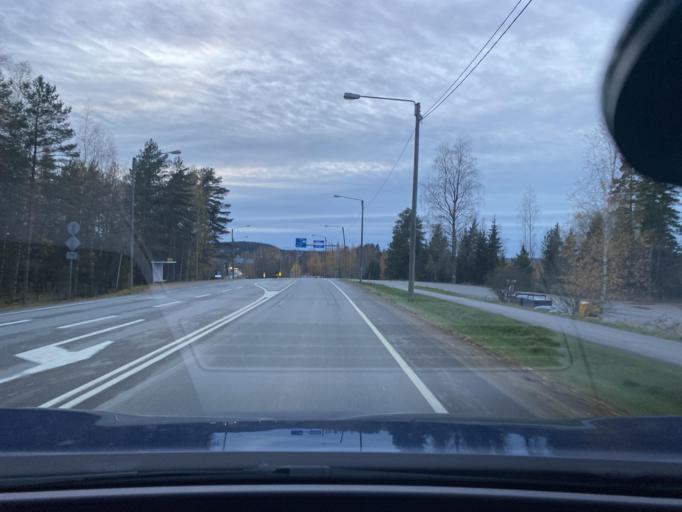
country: FI
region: Uusimaa
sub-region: Helsinki
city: Saukkola
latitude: 60.3819
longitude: 23.9740
